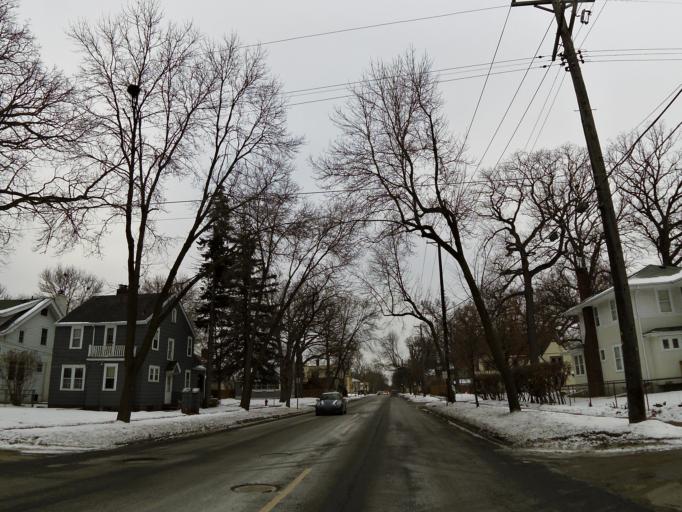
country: US
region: Minnesota
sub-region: Ramsey County
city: Falcon Heights
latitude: 44.9358
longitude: -93.1925
